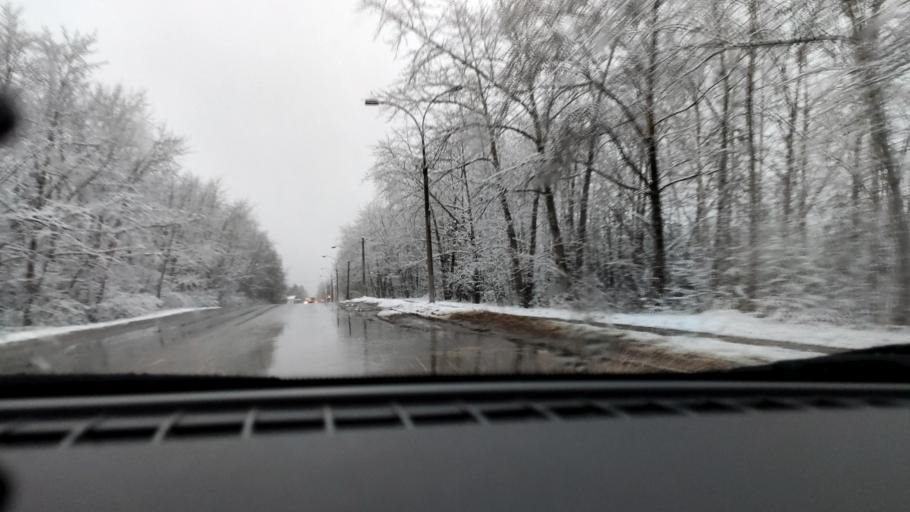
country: RU
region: Perm
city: Overyata
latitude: 58.0149
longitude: 55.9029
